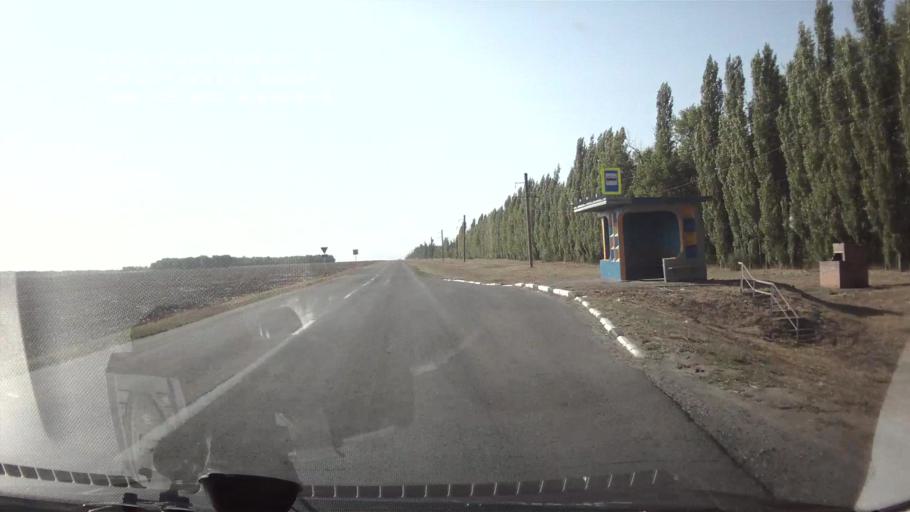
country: RU
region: Rostov
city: Tselina
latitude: 46.5351
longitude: 40.8998
